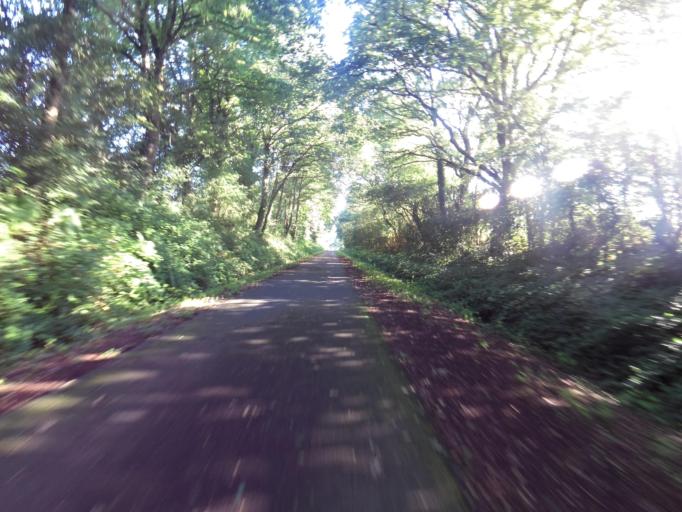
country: FR
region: Brittany
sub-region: Departement du Morbihan
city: Guillac
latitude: 47.8806
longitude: -2.4369
